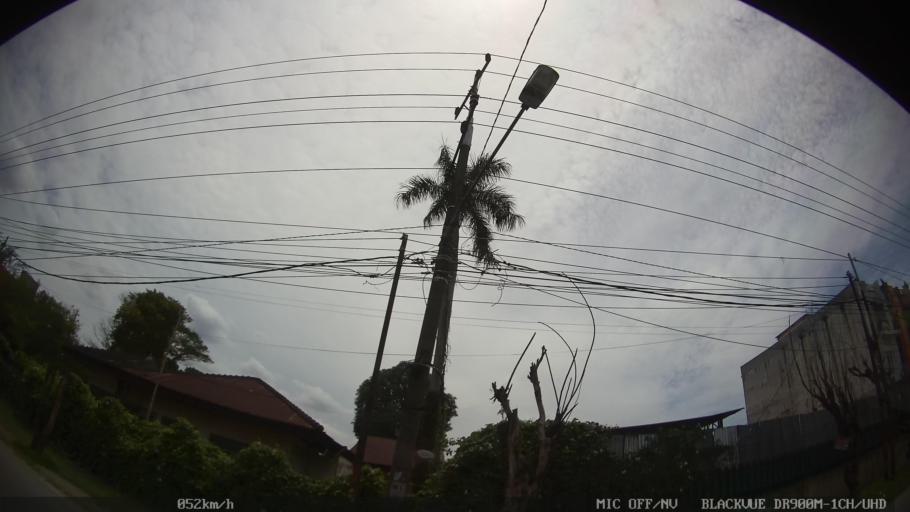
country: ID
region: North Sumatra
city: Sunggal
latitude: 3.5377
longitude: 98.6223
